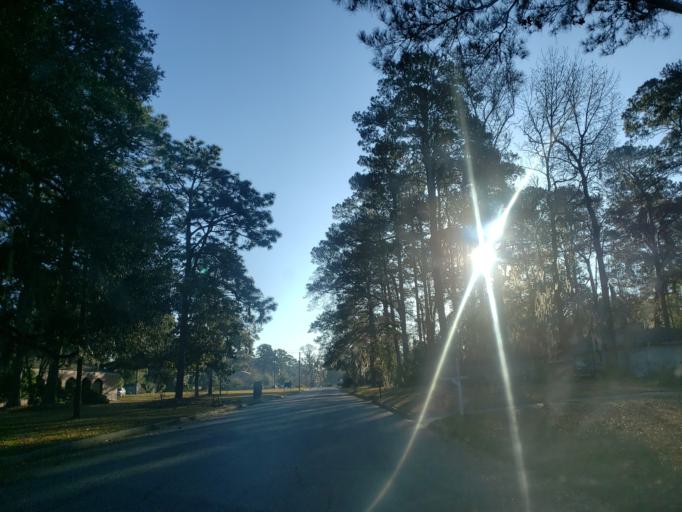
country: US
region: Georgia
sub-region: Chatham County
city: Isle of Hope
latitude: 32.0125
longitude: -81.1022
